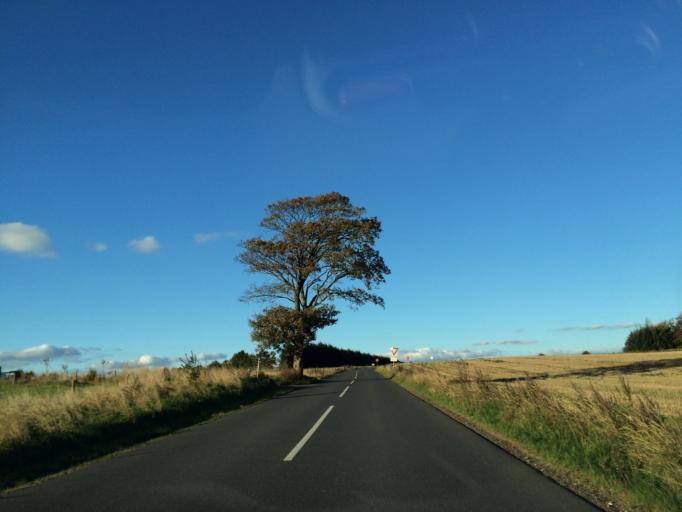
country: DK
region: Central Jutland
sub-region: Skanderborg Kommune
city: Ry
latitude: 56.1331
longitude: 9.7193
